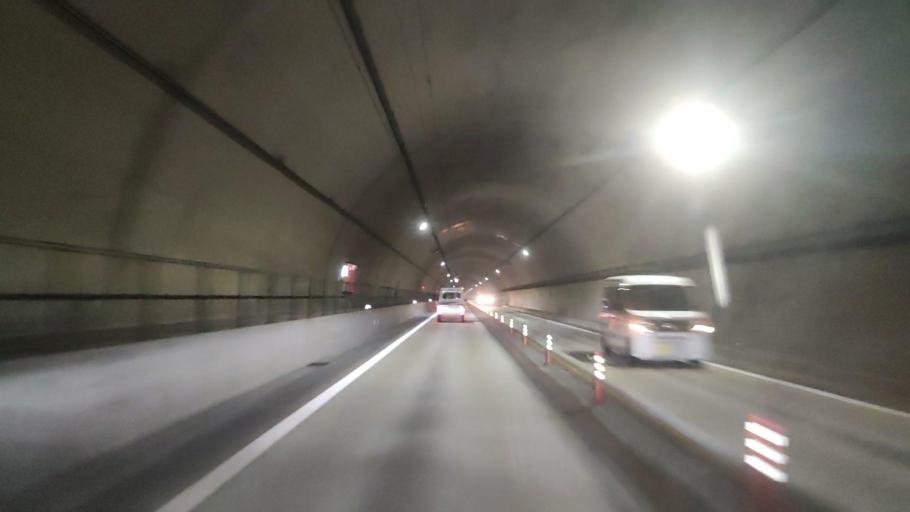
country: JP
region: Wakayama
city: Tanabe
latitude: 33.6206
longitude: 135.4201
